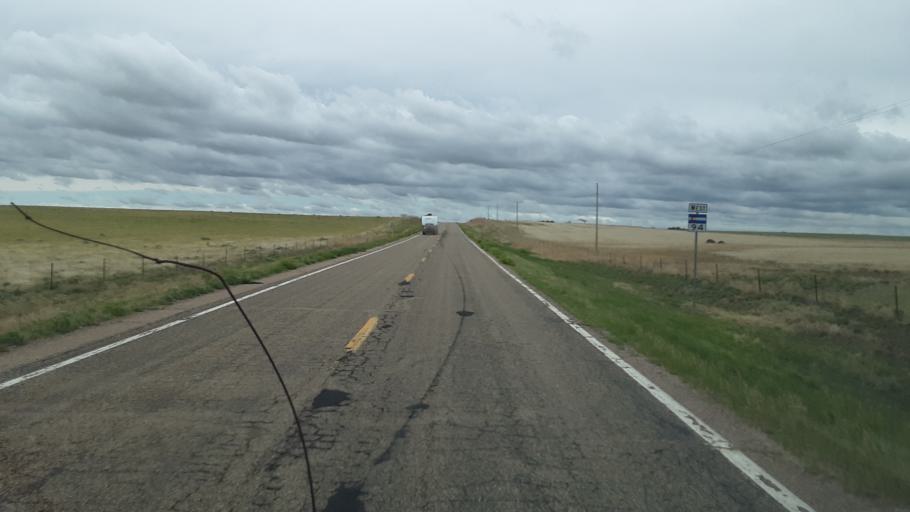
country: US
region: Colorado
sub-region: Lincoln County
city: Limon
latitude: 38.8384
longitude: -103.8699
